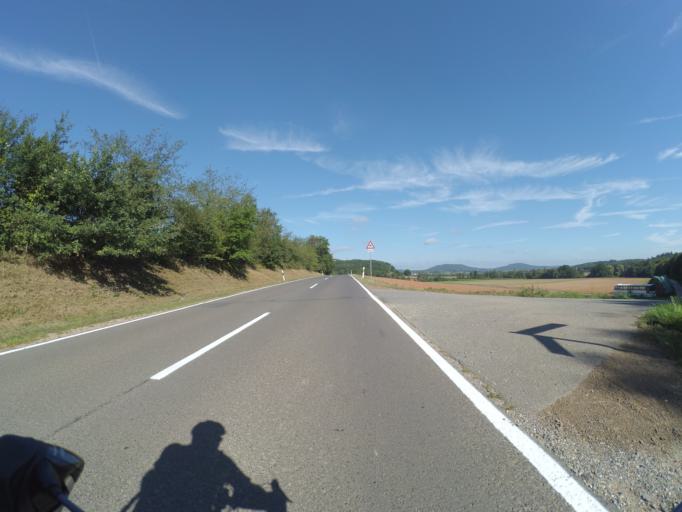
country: DE
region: Rheinland-Pfalz
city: Rivenich
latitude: 49.8824
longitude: 6.8457
